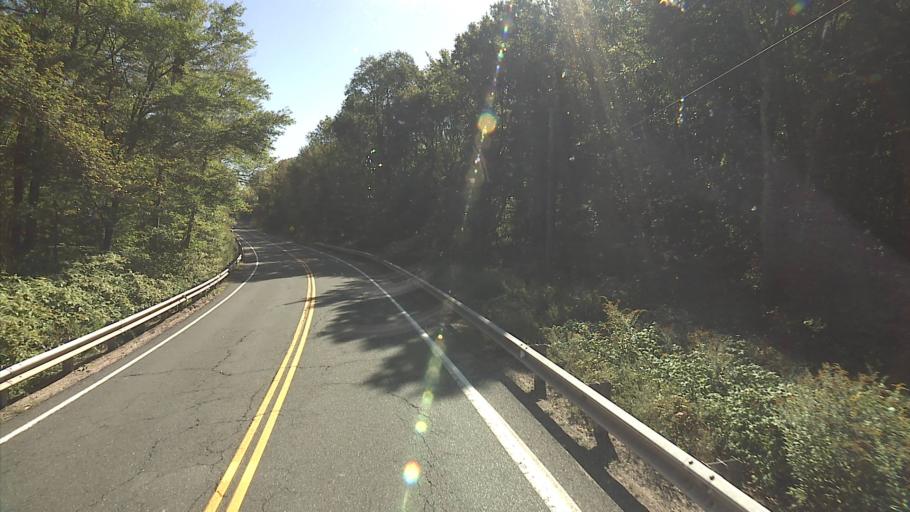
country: US
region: Connecticut
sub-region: Hartford County
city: Bristol
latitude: 41.7415
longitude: -72.9701
